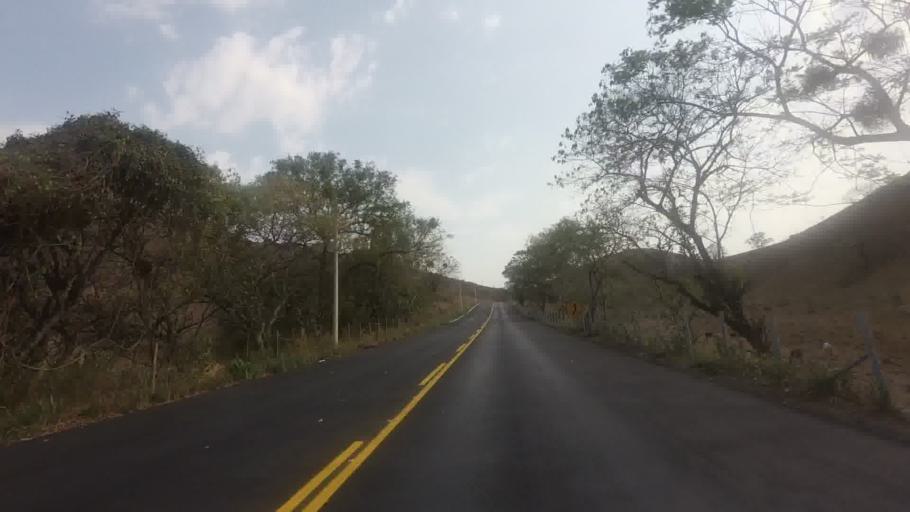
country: BR
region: Rio de Janeiro
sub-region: Bom Jesus Do Itabapoana
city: Bom Jesus do Itabapoana
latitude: -21.2392
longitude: -41.7527
